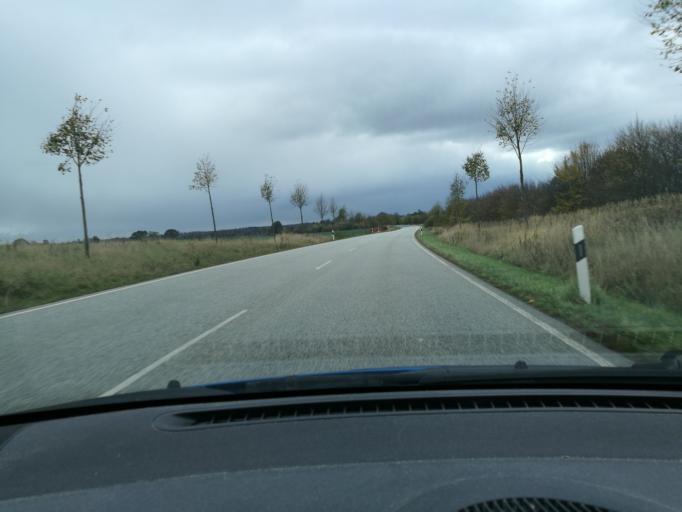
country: DE
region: Schleswig-Holstein
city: Harmsdorf
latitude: 53.6964
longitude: 10.7315
